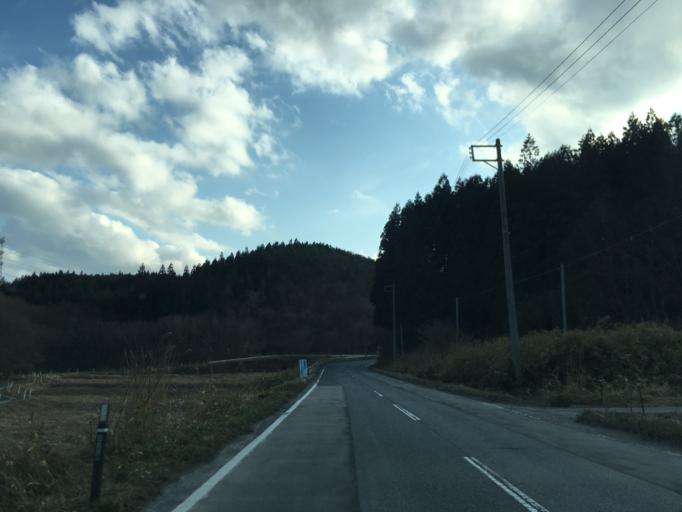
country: JP
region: Fukushima
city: Ishikawa
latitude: 37.1787
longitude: 140.6067
